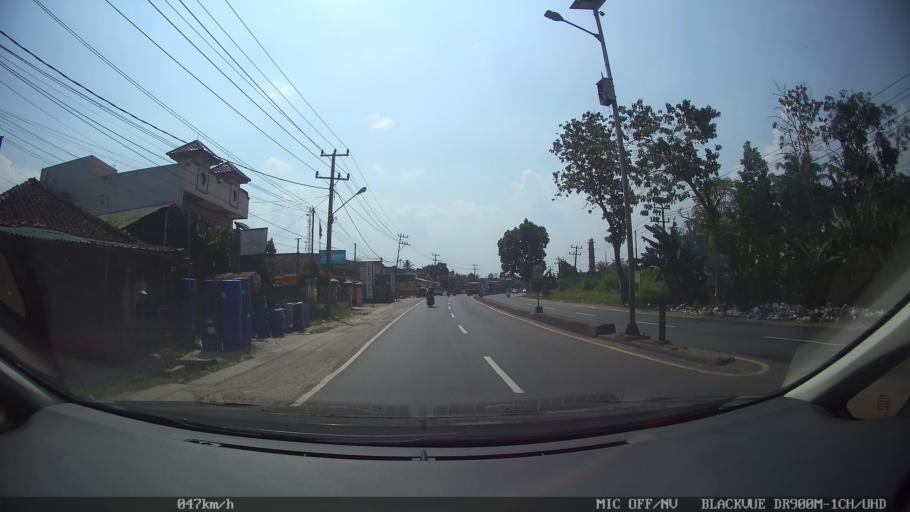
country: ID
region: Lampung
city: Natar
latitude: -5.3270
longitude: 105.2032
